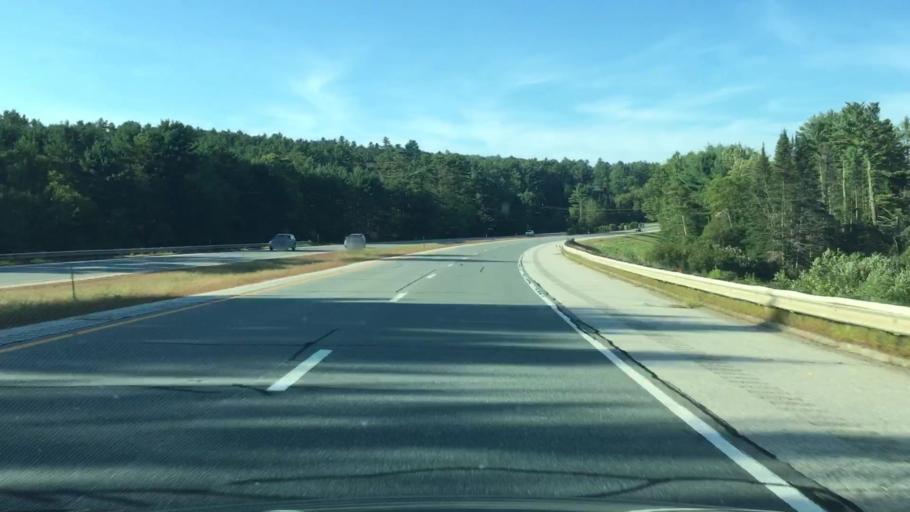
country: US
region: New Hampshire
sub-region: Grafton County
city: Littleton
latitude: 44.2474
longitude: -71.7611
